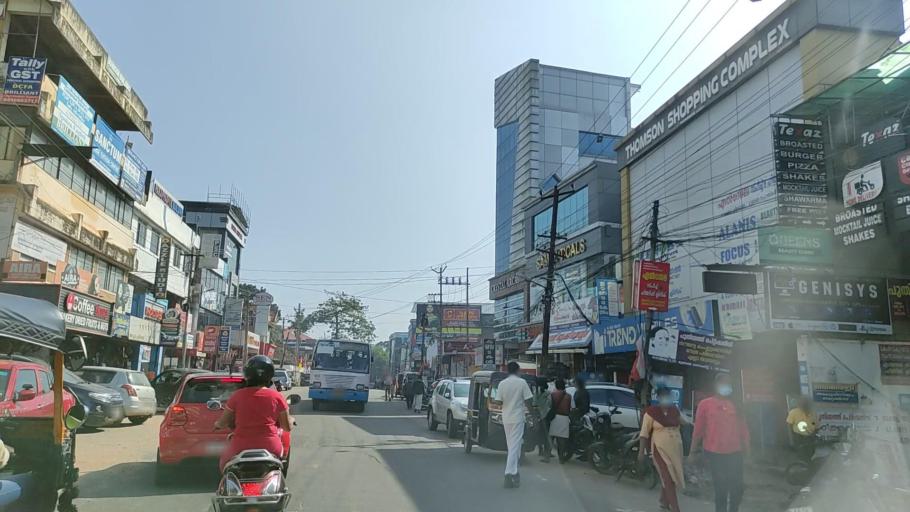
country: IN
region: Kerala
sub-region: Kollam
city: Punalur
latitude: 8.9264
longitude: 76.9171
